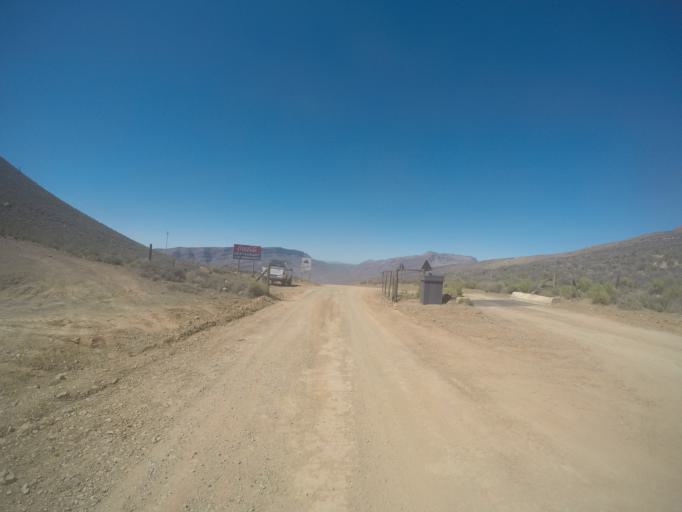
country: ZA
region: Western Cape
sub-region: West Coast District Municipality
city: Clanwilliam
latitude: -32.6105
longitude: 19.3675
